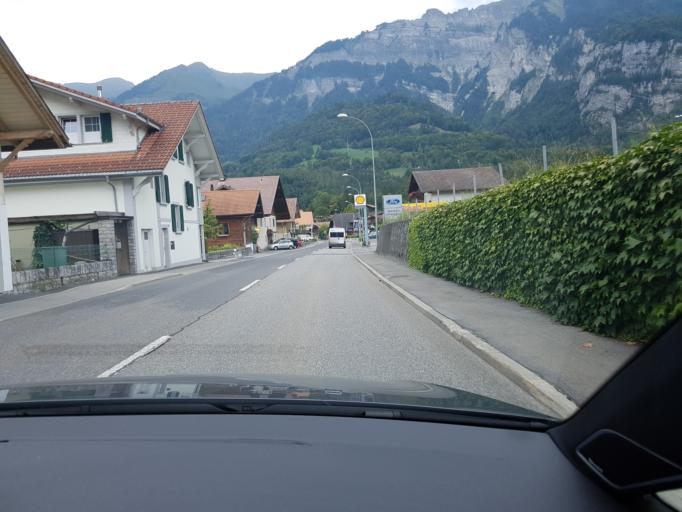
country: CH
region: Bern
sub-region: Interlaken-Oberhasli District
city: Brienz
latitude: 46.7486
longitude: 8.0538
